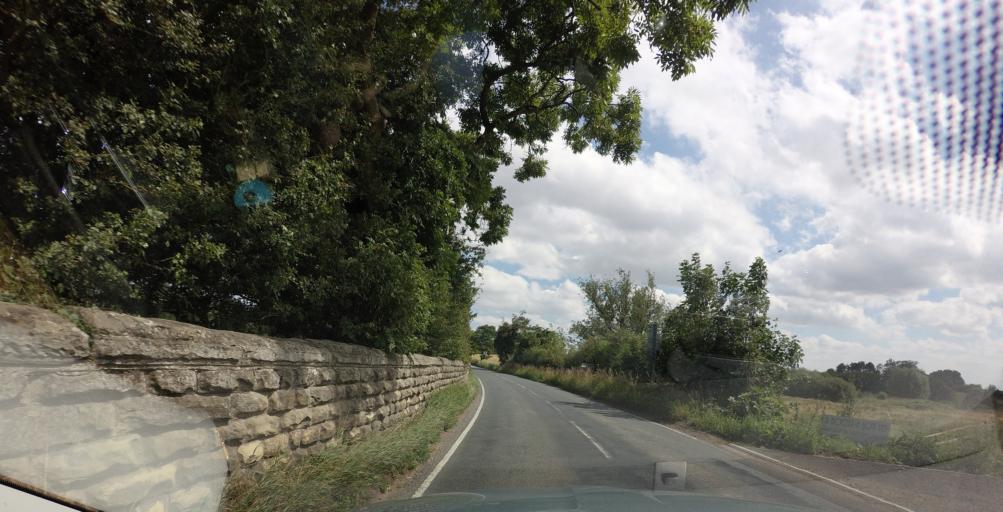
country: GB
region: England
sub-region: North Yorkshire
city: Ripon
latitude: 54.1417
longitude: -1.4920
